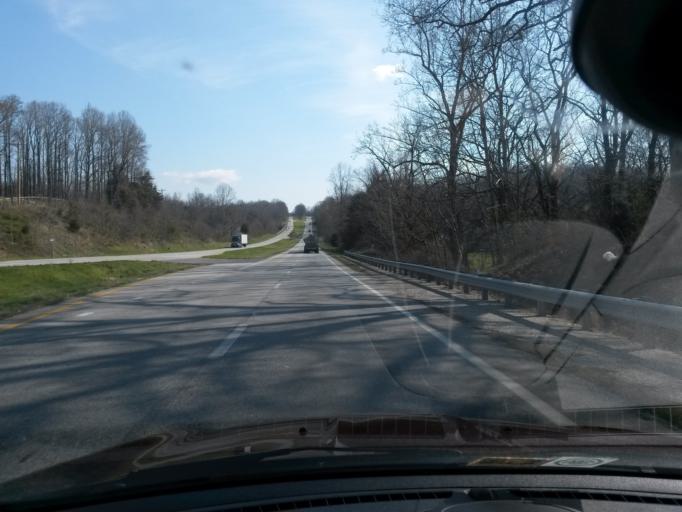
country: US
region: Virginia
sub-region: Amherst County
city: Amherst
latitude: 37.6246
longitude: -79.0081
